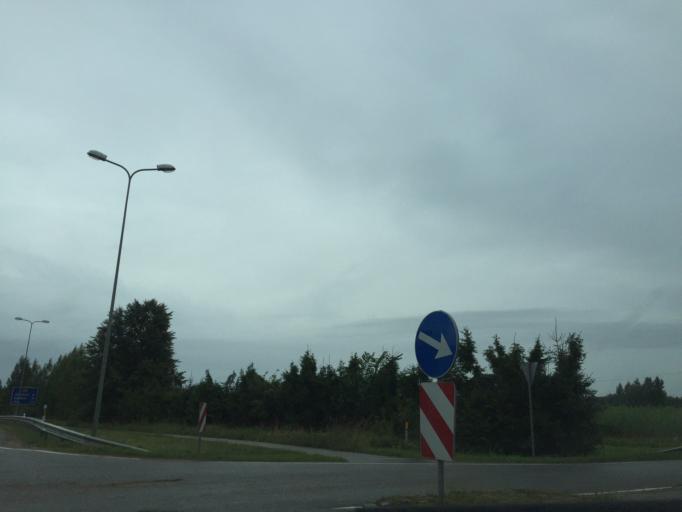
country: LV
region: Livani
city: Livani
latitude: 56.3893
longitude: 26.1523
